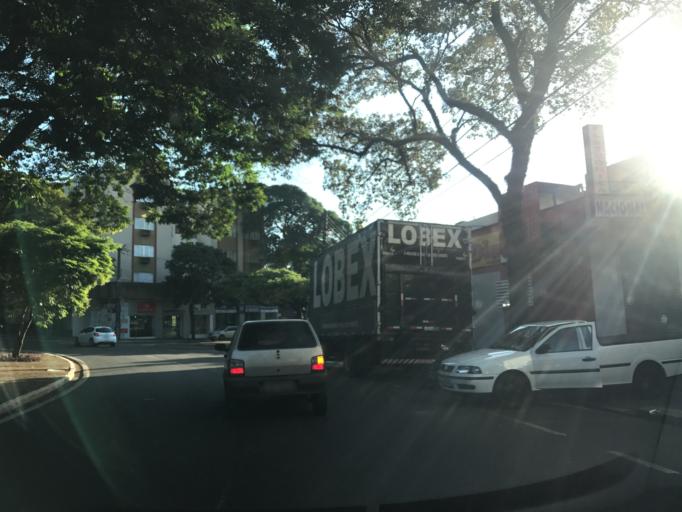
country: BR
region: Parana
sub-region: Maringa
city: Maringa
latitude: -23.4271
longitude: -51.9522
